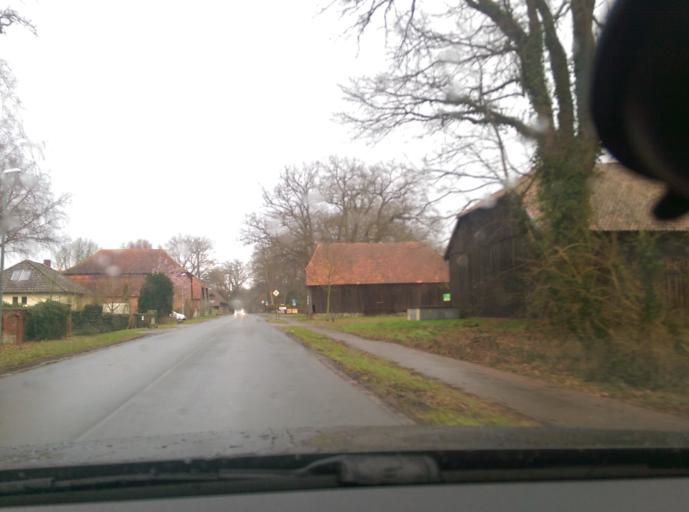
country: DE
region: Lower Saxony
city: Schwarmstedt
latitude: 52.6584
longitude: 9.6169
